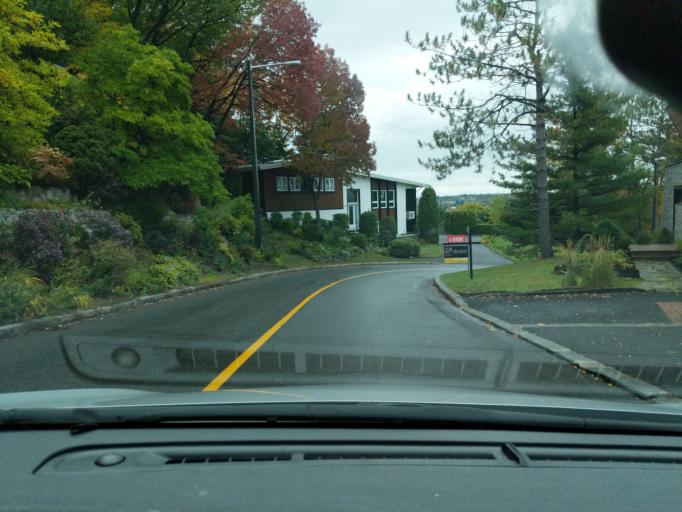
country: CA
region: Quebec
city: Quebec
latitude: 46.7635
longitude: -71.2670
